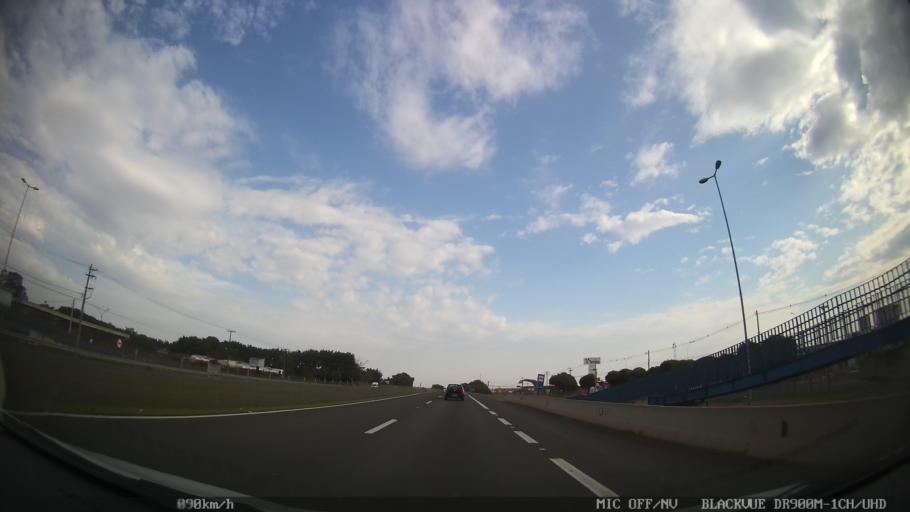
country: BR
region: Sao Paulo
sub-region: Paulinia
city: Paulinia
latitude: -22.7324
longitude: -47.1515
